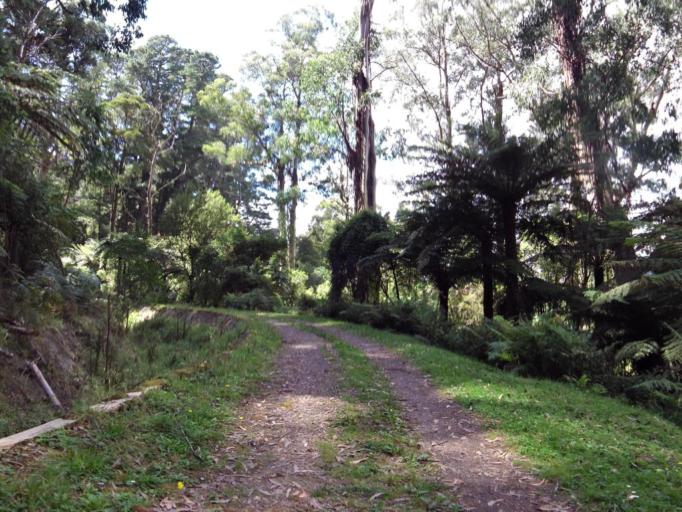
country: AU
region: Victoria
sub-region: Yarra Ranges
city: Millgrove
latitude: -37.7441
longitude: 145.6911
